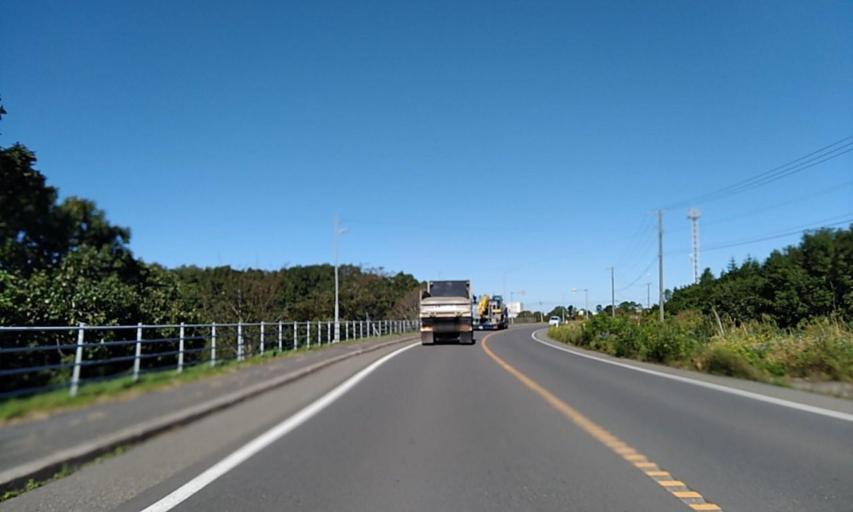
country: JP
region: Hokkaido
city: Shizunai-furukawacho
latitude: 42.4905
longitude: 142.0595
